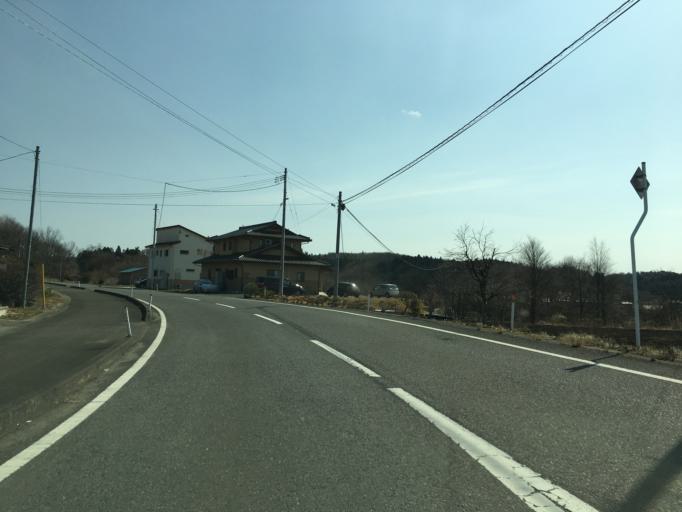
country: JP
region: Fukushima
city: Ishikawa
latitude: 37.1402
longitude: 140.3961
